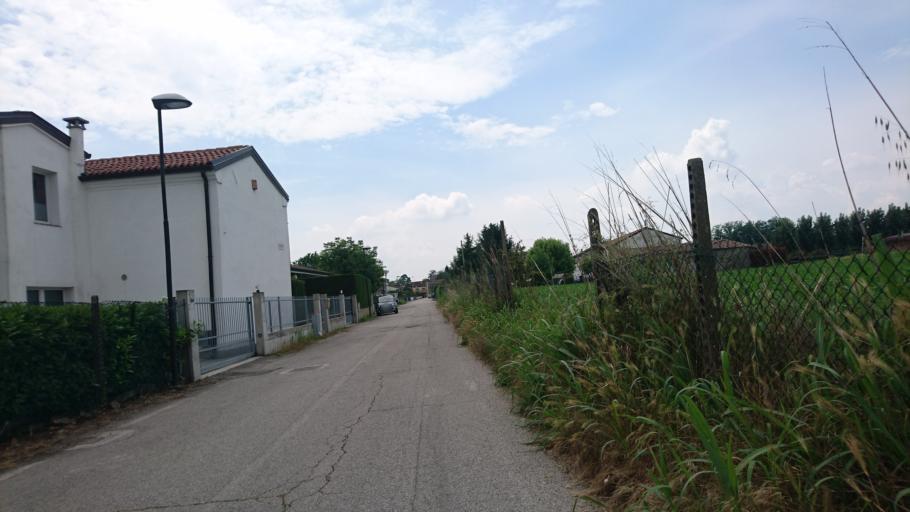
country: IT
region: Veneto
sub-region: Provincia di Rovigo
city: Baruchella
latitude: 45.0690
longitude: 11.4564
